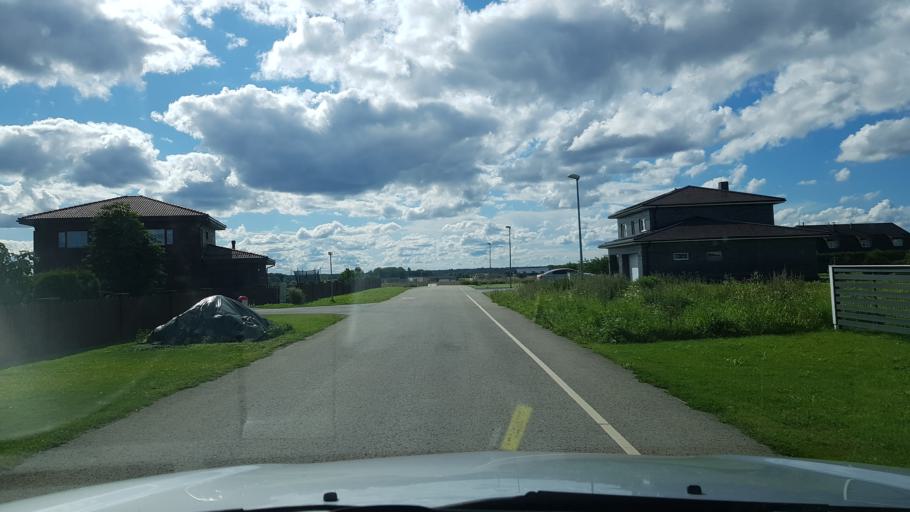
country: EE
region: Harju
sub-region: Kiili vald
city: Kiili
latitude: 59.3805
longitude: 24.8152
